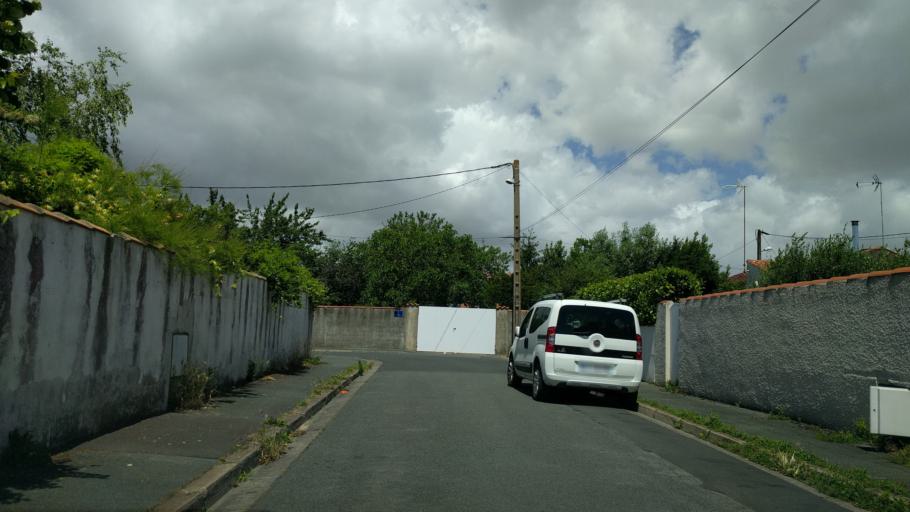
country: FR
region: Poitou-Charentes
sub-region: Departement de la Charente-Maritime
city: Puilboreau
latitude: 46.1682
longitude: -1.1287
